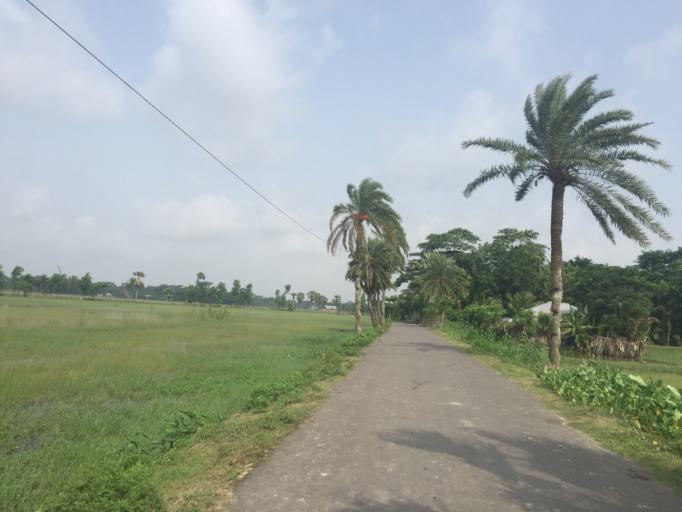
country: BD
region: Barisal
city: Mathba
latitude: 22.2115
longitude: 89.9249
